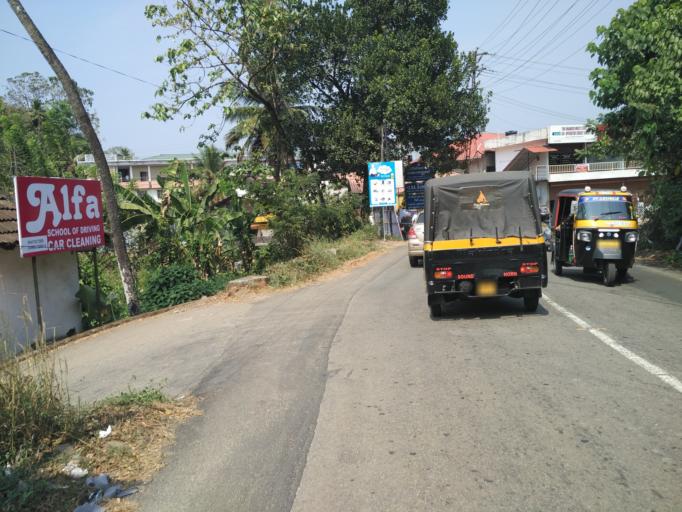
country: IN
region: Kerala
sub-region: Ernakulam
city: Muvattupuzha
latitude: 9.8927
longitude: 76.7065
